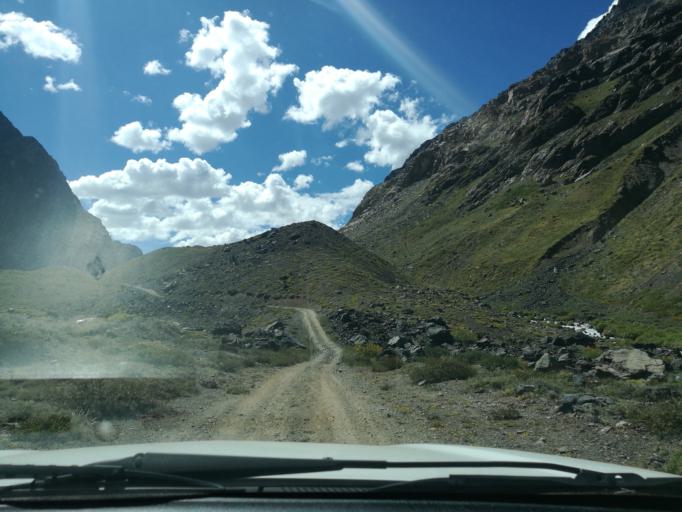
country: CL
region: O'Higgins
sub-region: Provincia de Cachapoal
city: Machali
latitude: -34.4139
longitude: -70.2218
